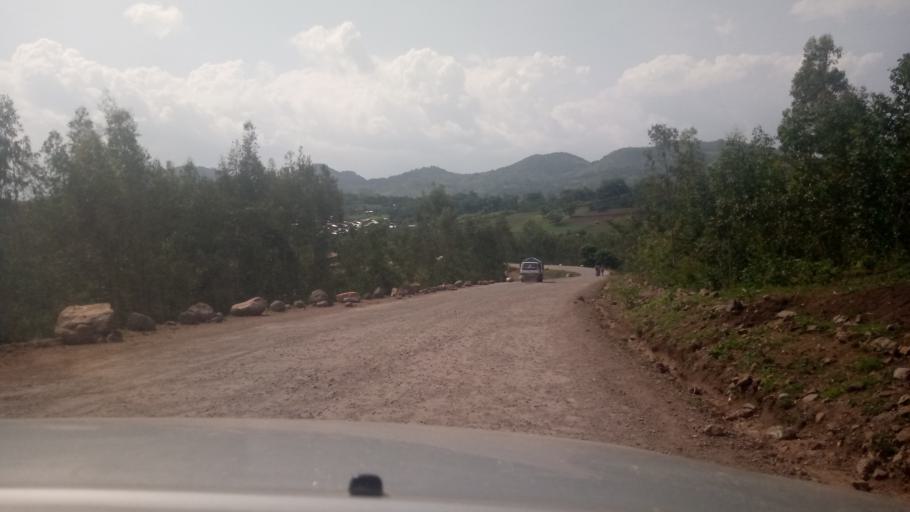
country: ET
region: Oromiya
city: Agaro
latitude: 7.9929
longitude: 36.5043
